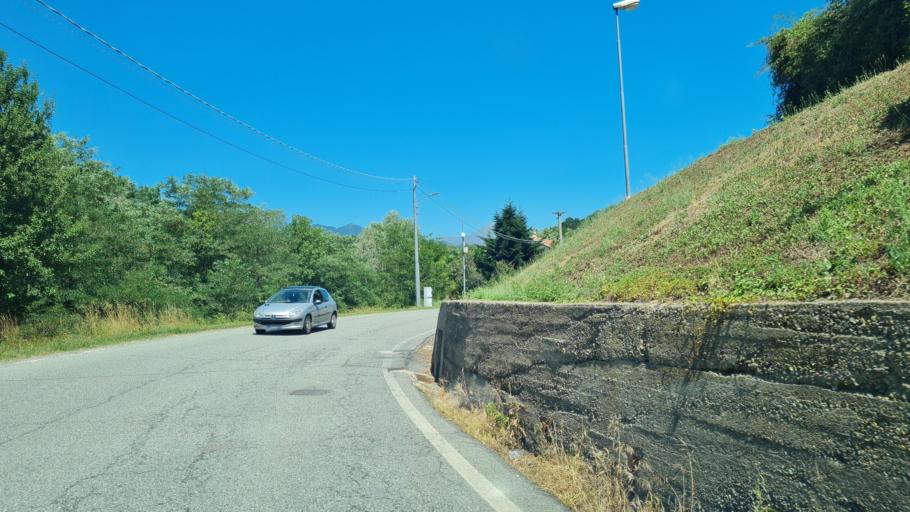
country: IT
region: Piedmont
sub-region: Provincia di Biella
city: Lessona
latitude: 45.5941
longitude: 8.1847
